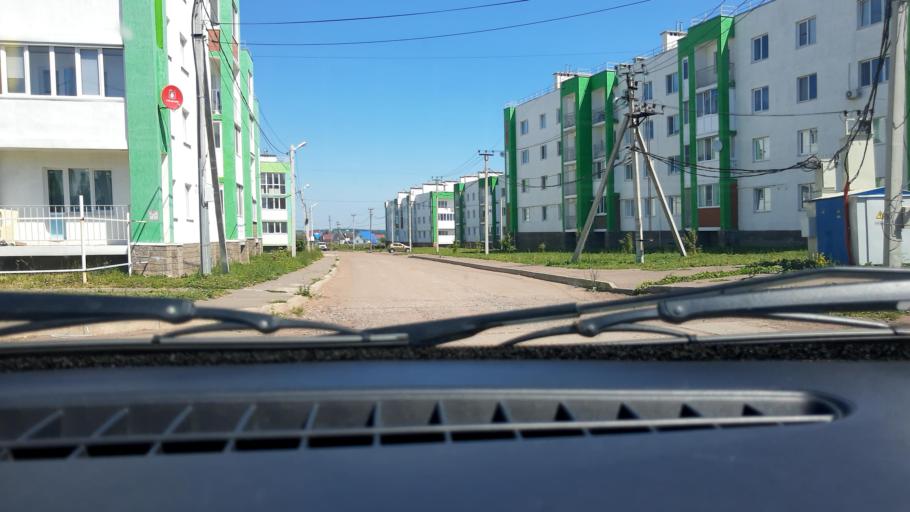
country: RU
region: Bashkortostan
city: Avdon
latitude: 54.4837
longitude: 55.8858
